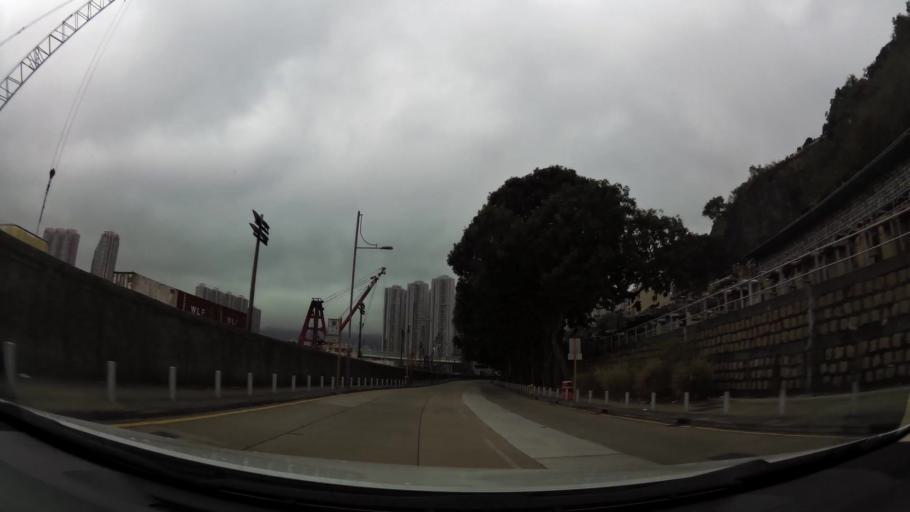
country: HK
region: Tsuen Wan
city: Tsuen Wan
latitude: 22.3568
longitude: 114.1152
